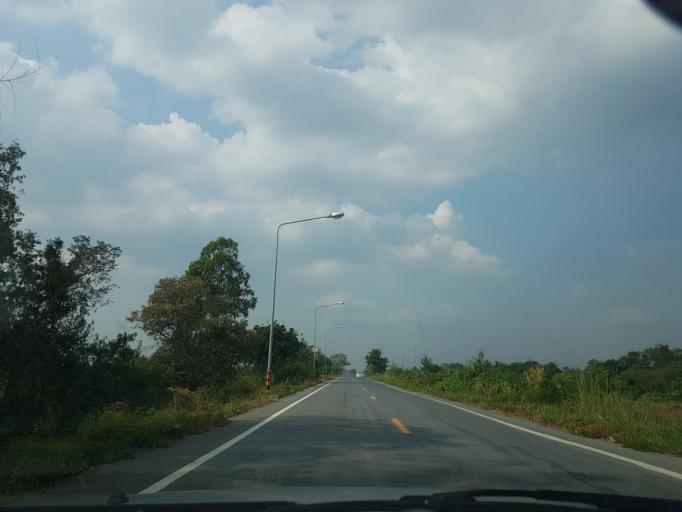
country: TH
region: Phra Nakhon Si Ayutthaya
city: Phachi
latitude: 14.4582
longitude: 100.7563
